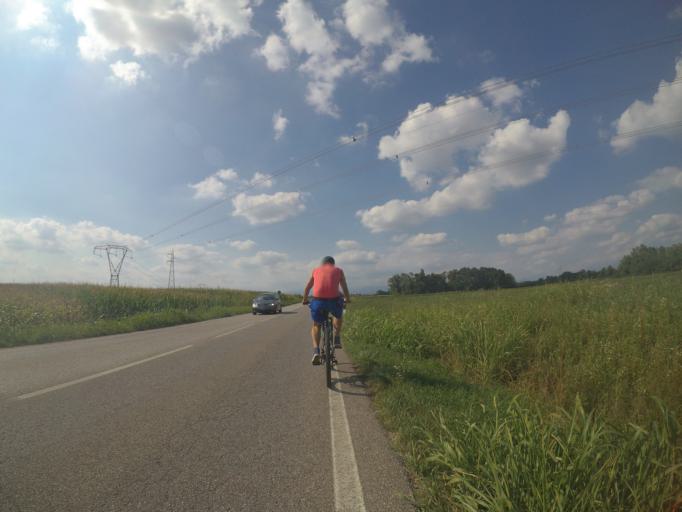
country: IT
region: Friuli Venezia Giulia
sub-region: Provincia di Udine
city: Basiliano-Vissandone
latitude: 46.0473
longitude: 13.0933
